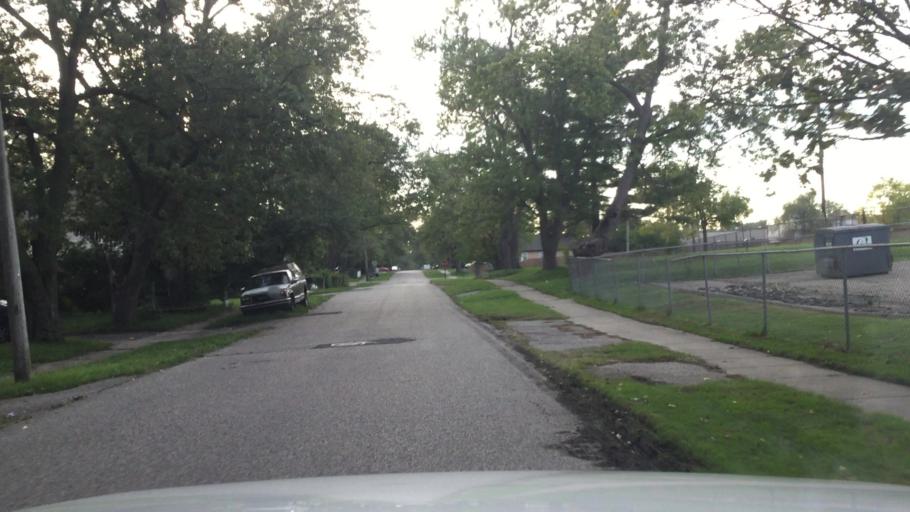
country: US
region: Michigan
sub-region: Oakland County
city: Sylvan Lake
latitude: 42.6343
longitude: -83.3275
